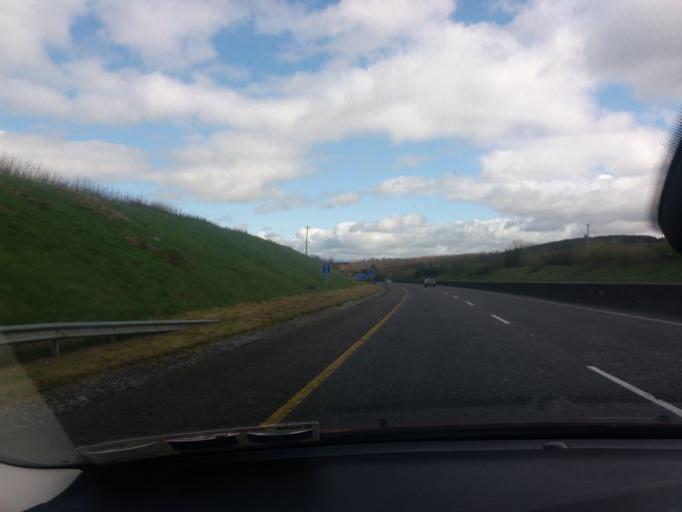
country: IE
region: Munster
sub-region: County Cork
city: Fermoy
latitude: 52.1082
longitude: -8.2749
